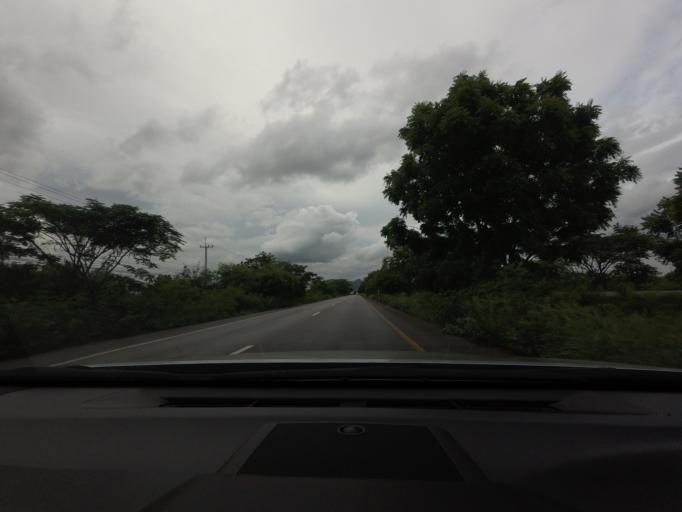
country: TH
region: Phetchaburi
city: Cha-am
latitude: 12.7623
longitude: 99.9338
